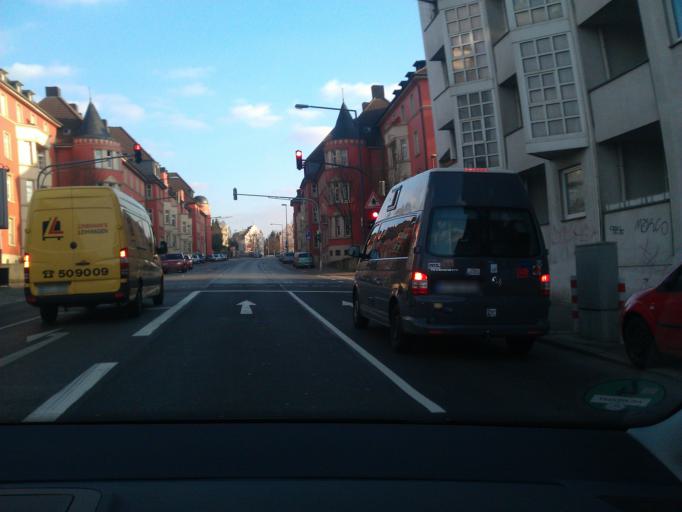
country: DE
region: North Rhine-Westphalia
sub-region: Regierungsbezirk Koln
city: Aachen
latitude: 50.7789
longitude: 6.1097
